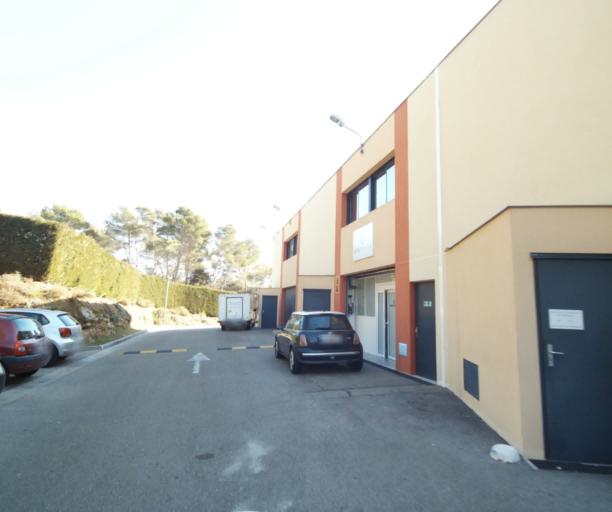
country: FR
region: Provence-Alpes-Cote d'Azur
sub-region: Departement des Alpes-Maritimes
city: Biot
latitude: 43.6097
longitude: 7.0708
